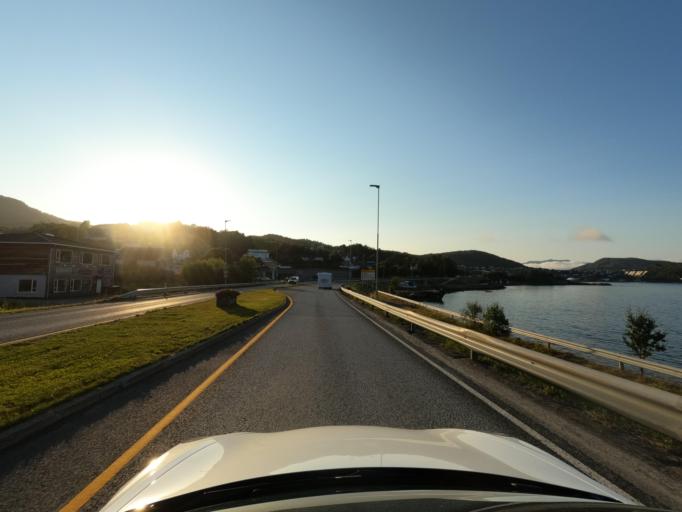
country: NO
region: Troms
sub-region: Harstad
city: Harstad
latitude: 68.7618
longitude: 16.5623
